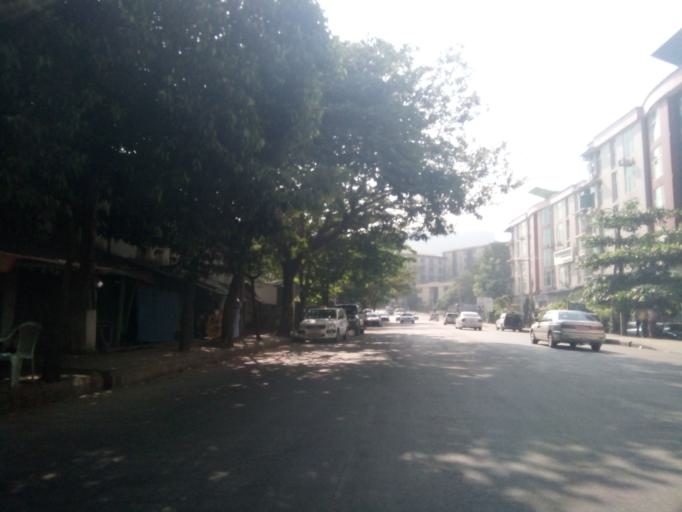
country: MM
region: Yangon
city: Yangon
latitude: 16.8211
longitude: 96.1239
